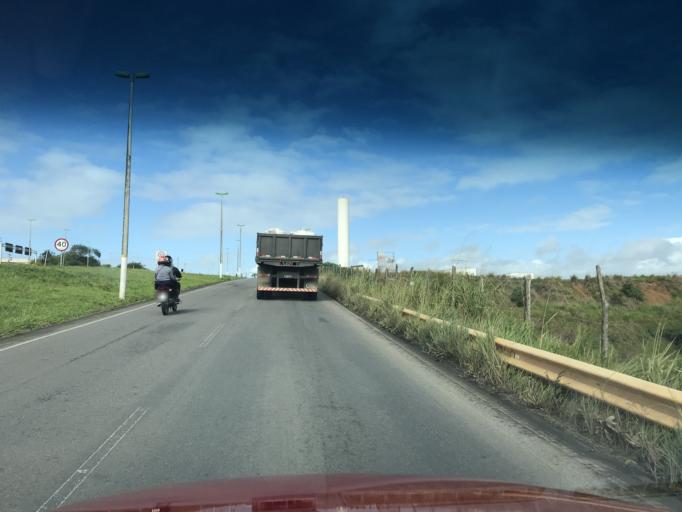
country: BR
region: Bahia
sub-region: Santo Antonio De Jesus
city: Santo Antonio de Jesus
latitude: -12.9630
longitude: -39.2718
